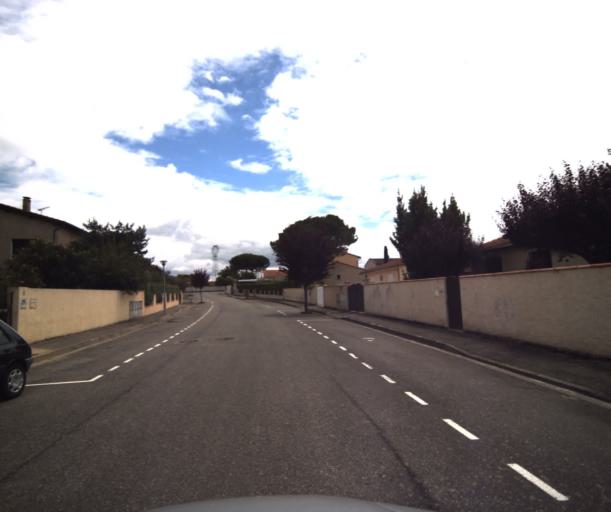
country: FR
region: Midi-Pyrenees
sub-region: Departement de la Haute-Garonne
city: Roquettes
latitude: 43.4983
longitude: 1.3742
